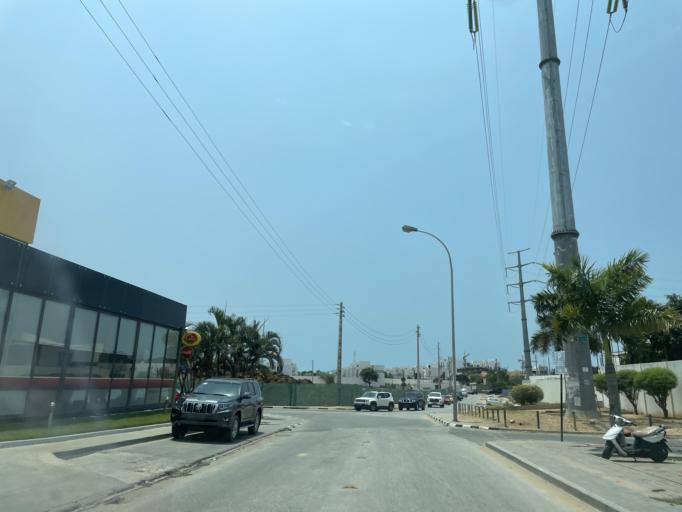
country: AO
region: Luanda
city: Luanda
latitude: -8.9073
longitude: 13.1958
